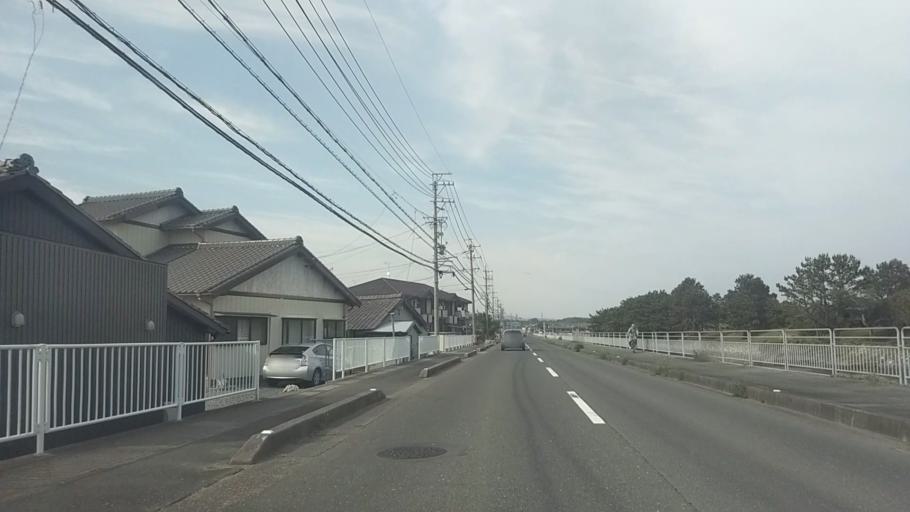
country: JP
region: Shizuoka
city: Kosai-shi
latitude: 34.7174
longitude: 137.5917
